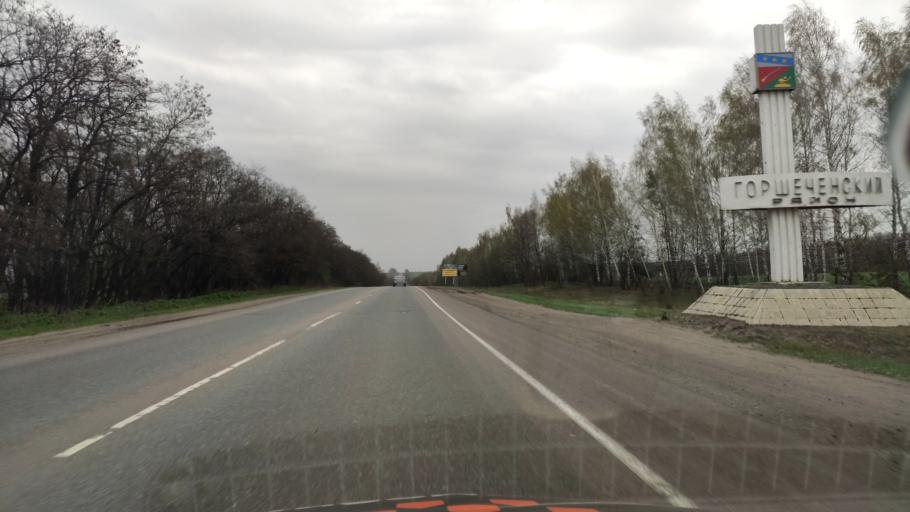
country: RU
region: Belgorod
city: Staryy Oskol
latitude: 51.4287
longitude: 37.8979
